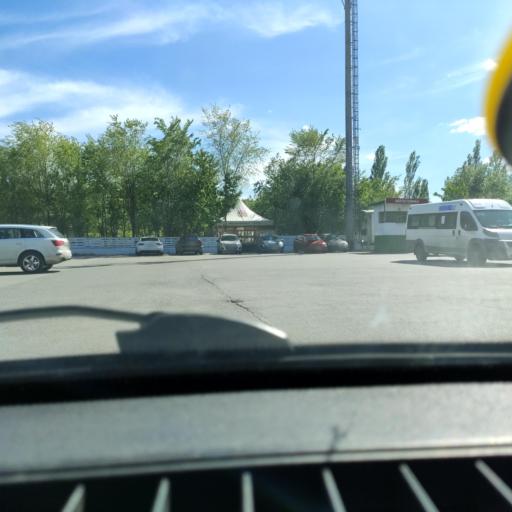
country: RU
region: Samara
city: Tol'yatti
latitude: 53.4977
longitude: 49.2874
